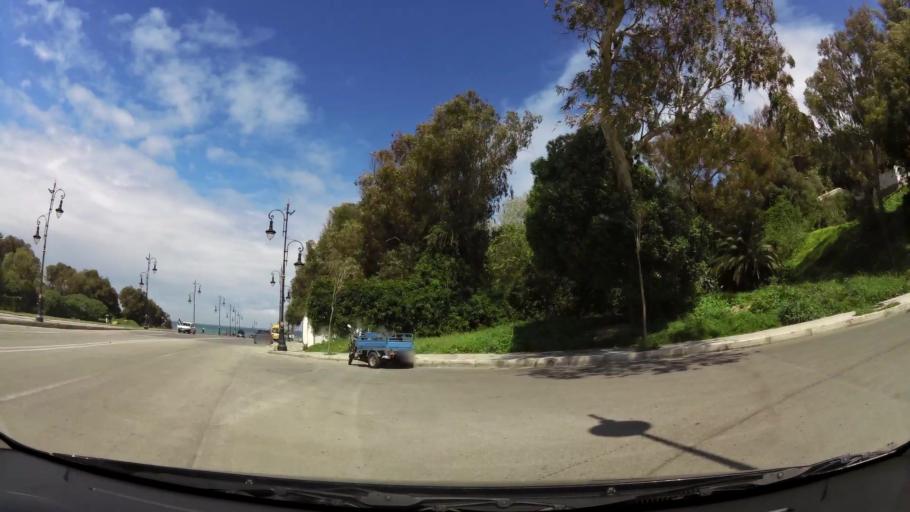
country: MA
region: Tanger-Tetouan
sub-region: Tanger-Assilah
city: Tangier
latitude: 35.7912
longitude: -5.8337
